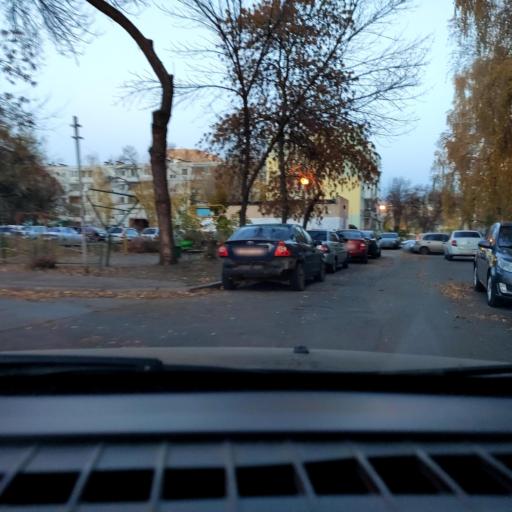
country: RU
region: Samara
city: Tol'yatti
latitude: 53.5199
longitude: 49.2925
